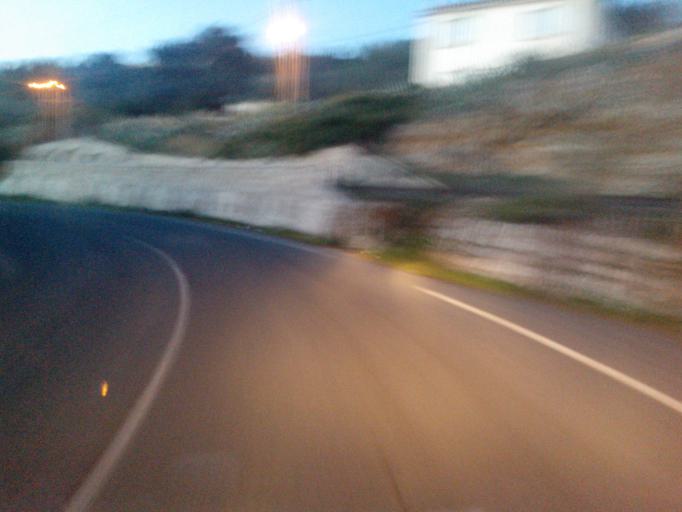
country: FR
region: Languedoc-Roussillon
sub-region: Departement des Pyrenees-Orientales
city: Estagel
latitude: 42.7775
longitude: 2.6968
